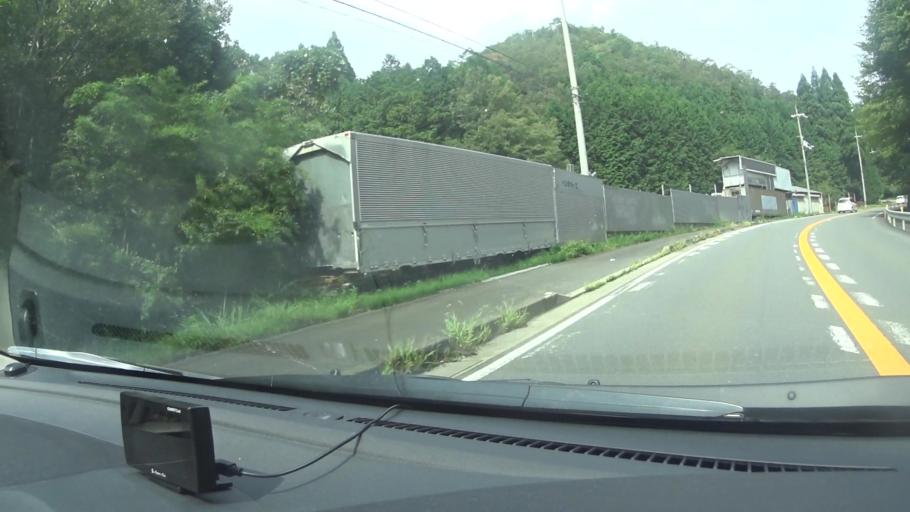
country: JP
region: Hyogo
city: Sasayama
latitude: 35.1646
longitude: 135.3590
